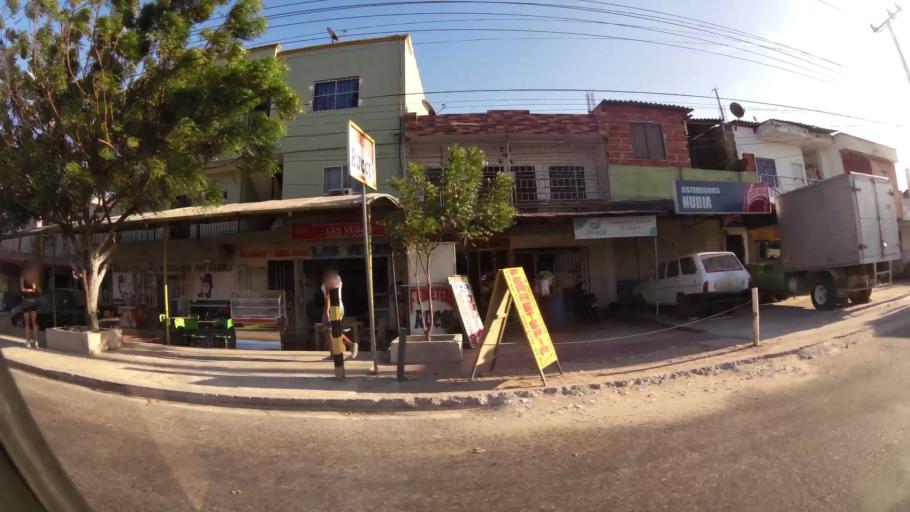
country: CO
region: Atlantico
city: Soledad
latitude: 10.9244
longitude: -74.7923
